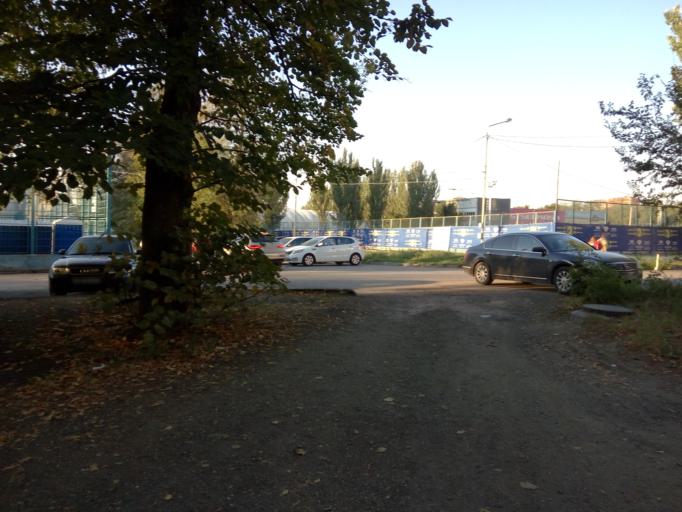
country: RU
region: Rostov
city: Rostov-na-Donu
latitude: 47.2436
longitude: 39.7587
